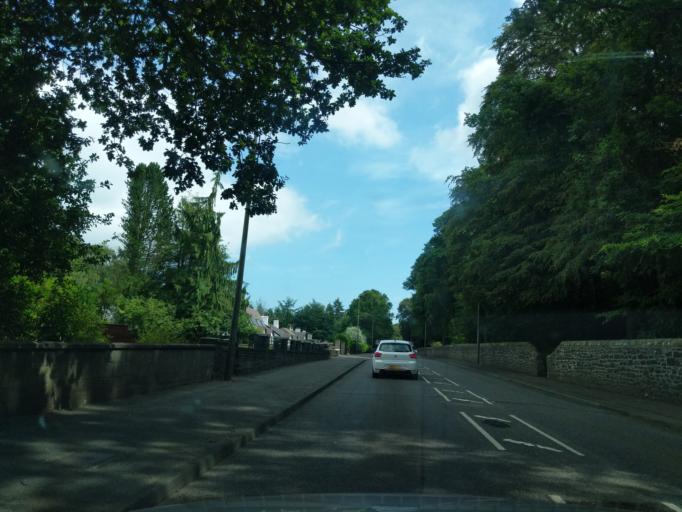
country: GB
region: Scotland
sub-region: Angus
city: Muirhead
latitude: 56.4923
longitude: -3.0499
